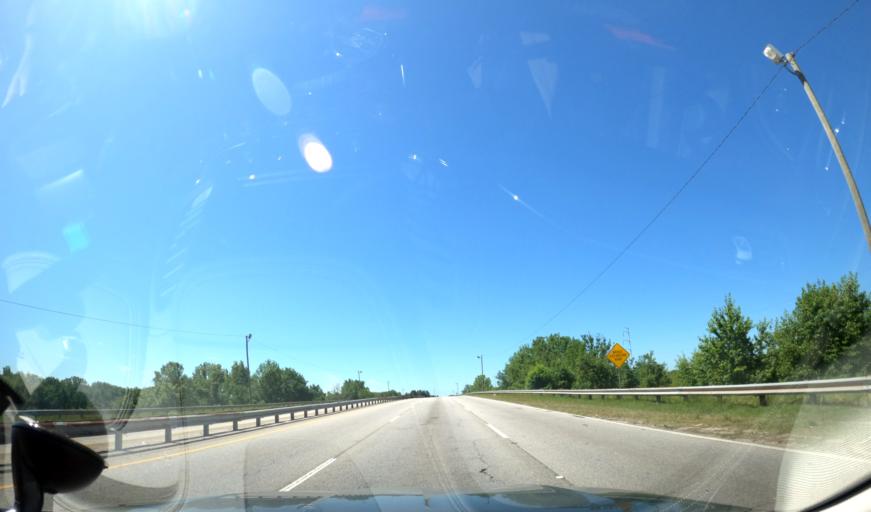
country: US
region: Georgia
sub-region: Richmond County
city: Augusta
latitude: 33.4477
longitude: -81.9765
